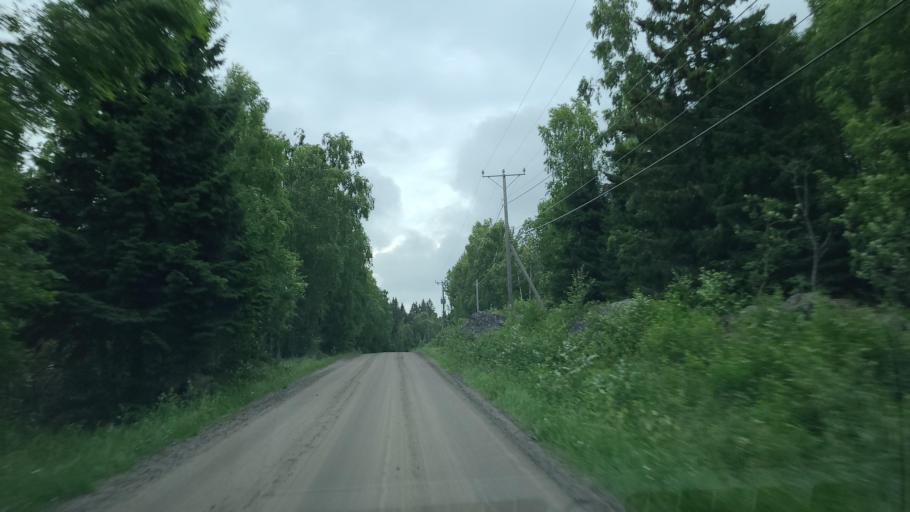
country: FI
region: Ostrobothnia
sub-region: Vaasa
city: Replot
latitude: 63.3043
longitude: 21.1539
